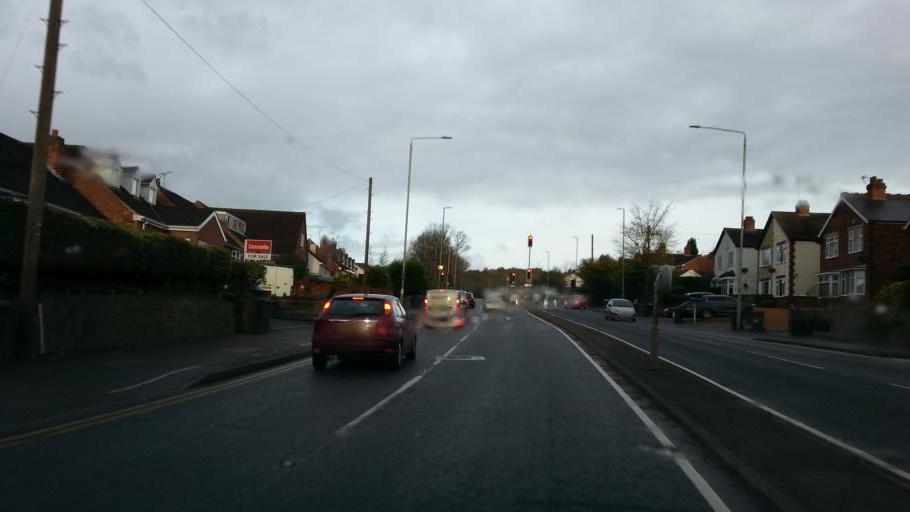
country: GB
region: England
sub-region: Leicestershire
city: Markfield
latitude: 52.6677
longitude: -1.2409
